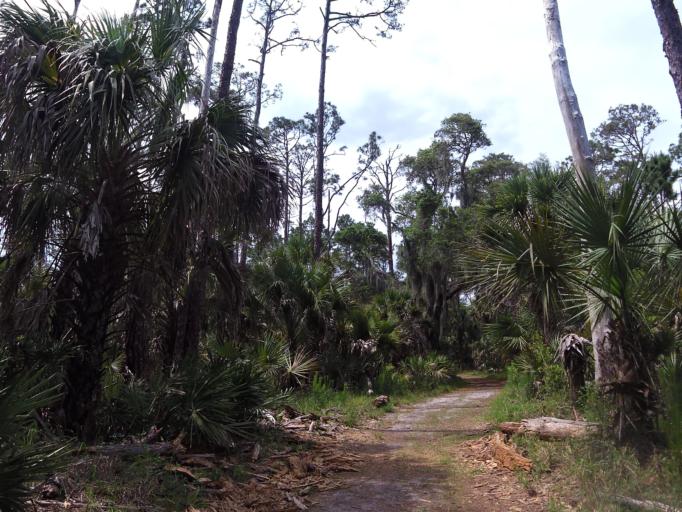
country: US
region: Florida
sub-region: Flagler County
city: Flagler Beach
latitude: 29.4057
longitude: -81.1232
